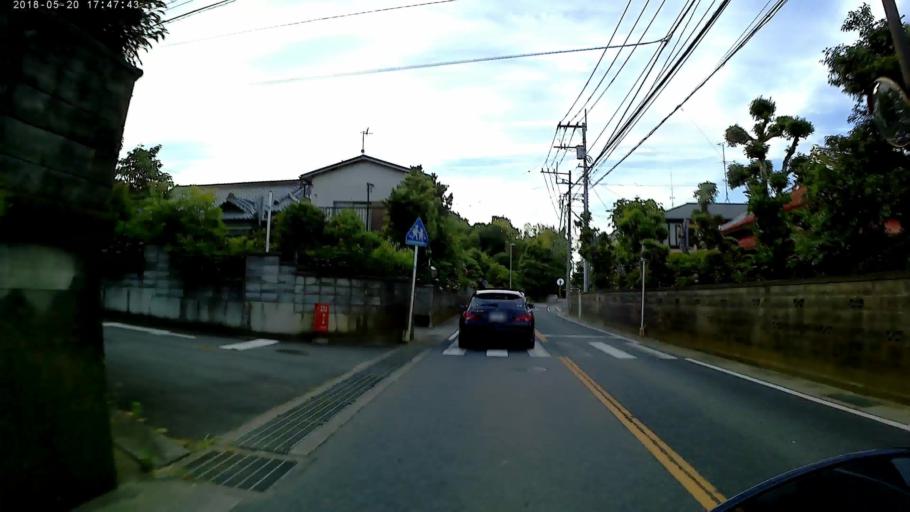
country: JP
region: Kanagawa
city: Oiso
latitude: 35.3357
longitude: 139.2931
